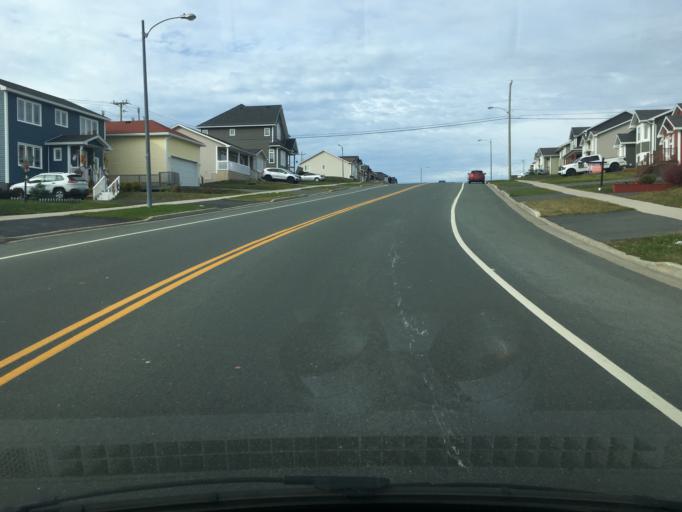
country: CA
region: Newfoundland and Labrador
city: Mount Pearl
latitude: 47.5494
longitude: -52.7883
